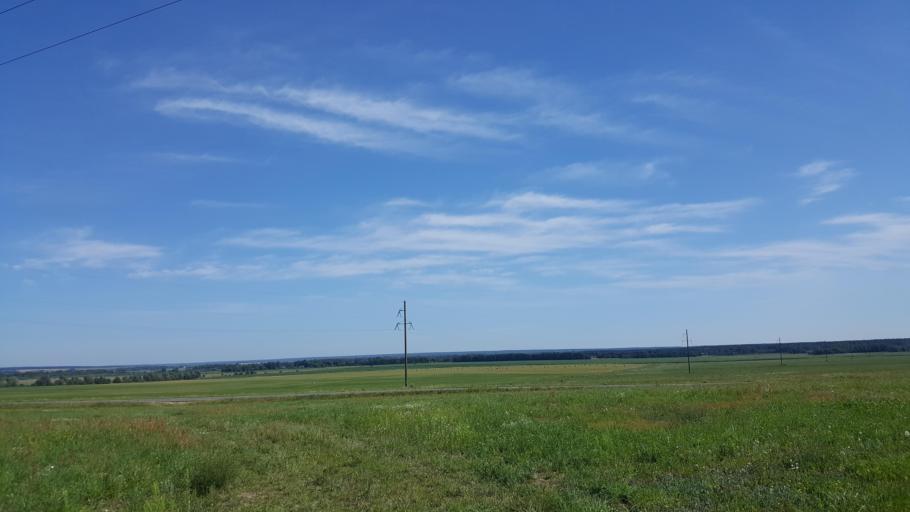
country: BY
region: Brest
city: Kamyanyets
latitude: 52.4044
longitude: 23.8604
